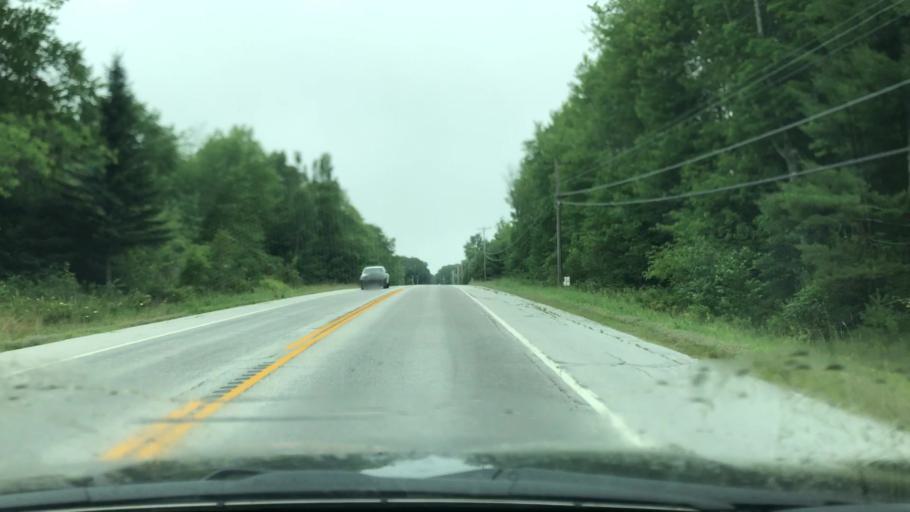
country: US
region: Maine
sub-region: Waldo County
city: Northport
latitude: 44.3256
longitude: -68.9606
